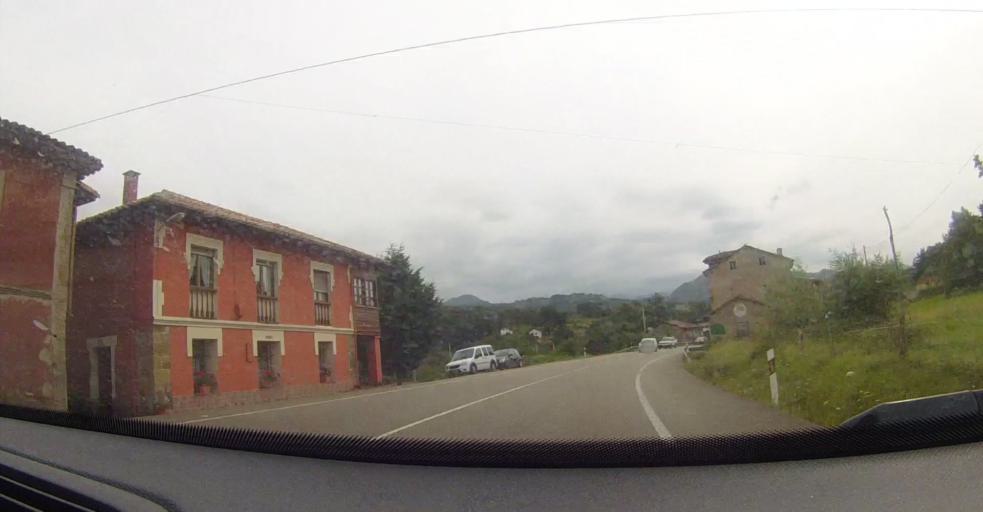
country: ES
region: Asturias
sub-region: Province of Asturias
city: Parres
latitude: 43.3699
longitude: -5.1838
